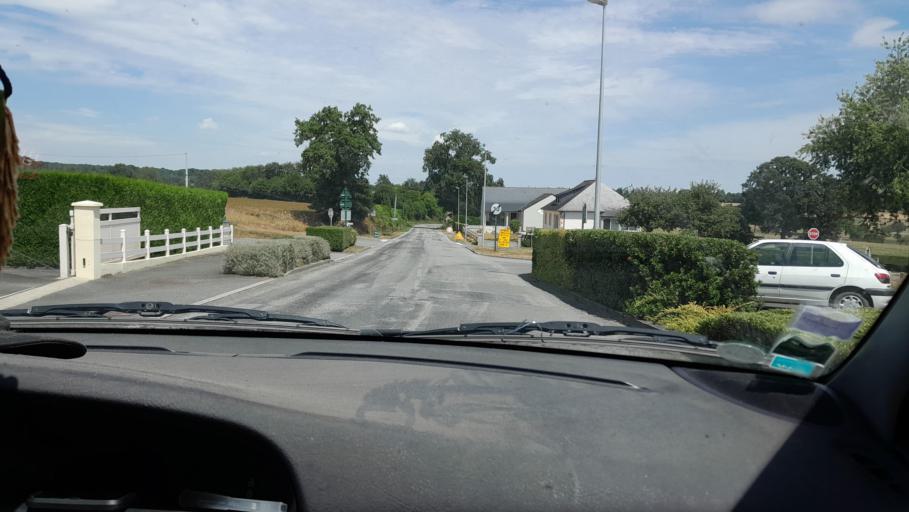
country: FR
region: Brittany
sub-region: Departement d'Ille-et-Vilaine
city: Le Pertre
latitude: 48.0375
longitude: -1.0368
